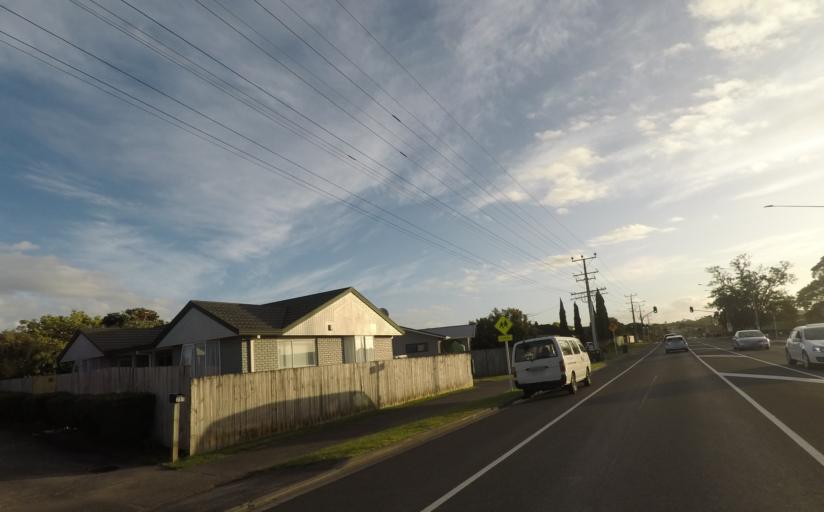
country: NZ
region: Auckland
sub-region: Auckland
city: Rosebank
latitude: -36.8046
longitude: 174.6382
